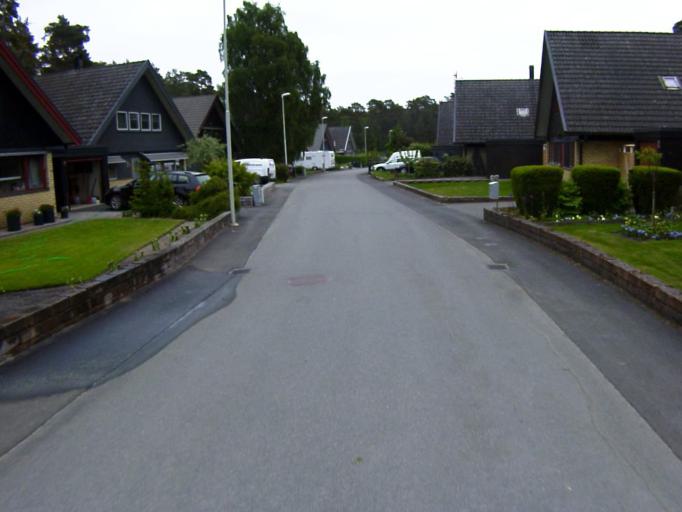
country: SE
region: Skane
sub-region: Kristianstads Kommun
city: Ahus
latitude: 55.9110
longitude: 14.2775
